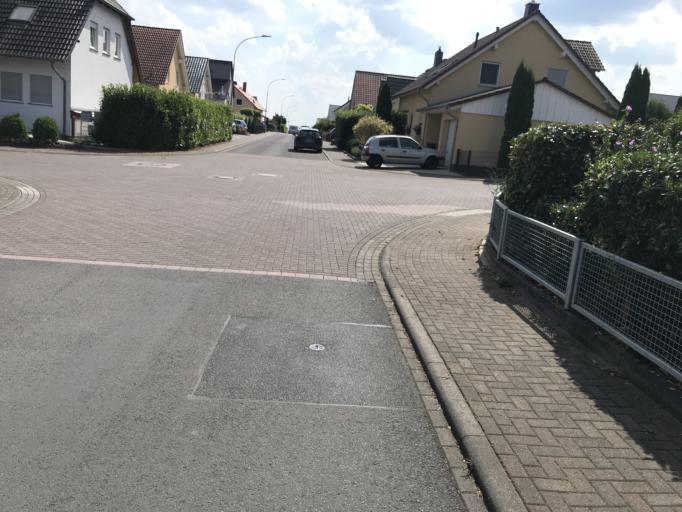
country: DE
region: Hesse
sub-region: Regierungsbezirk Darmstadt
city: Wolfersheim
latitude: 50.3918
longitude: 8.8029
